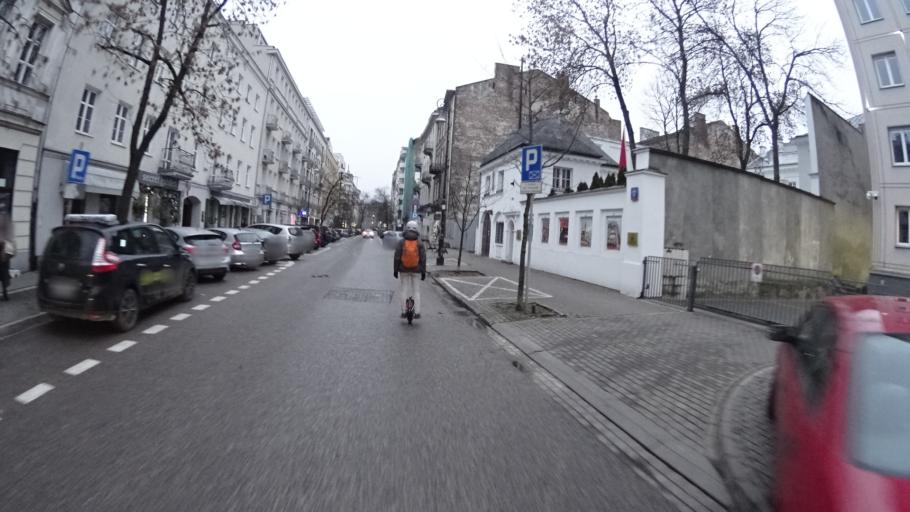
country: PL
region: Masovian Voivodeship
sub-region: Warszawa
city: Warsaw
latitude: 52.2246
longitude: 21.0076
